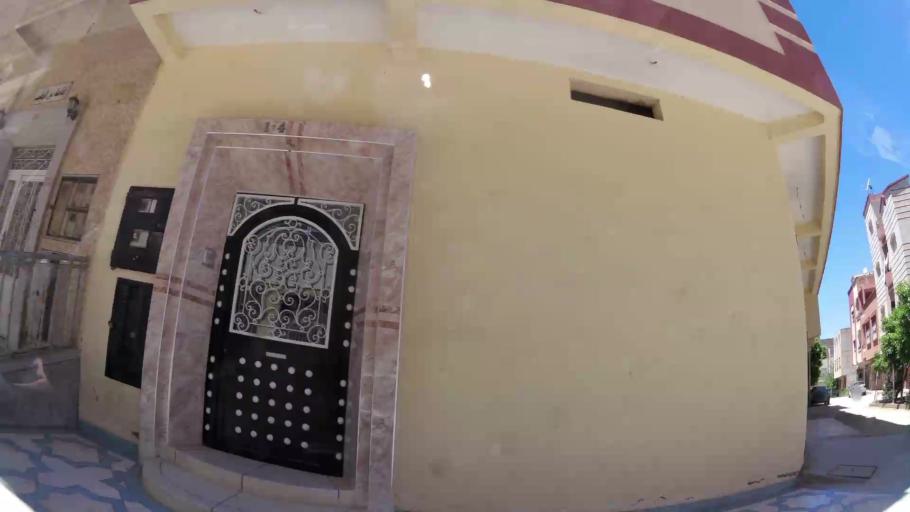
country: MA
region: Meknes-Tafilalet
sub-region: Meknes
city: Meknes
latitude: 33.8572
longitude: -5.5518
